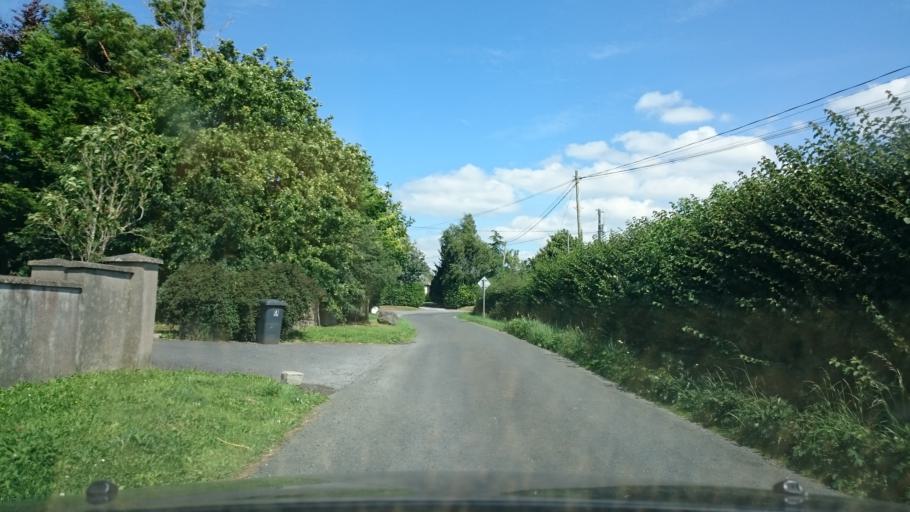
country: IE
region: Leinster
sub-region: Kilkenny
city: Thomastown
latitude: 52.6455
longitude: -7.1155
